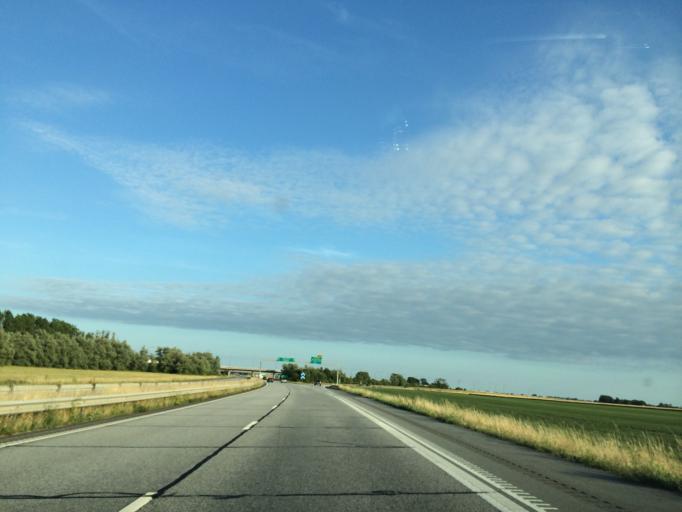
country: SE
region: Skane
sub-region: Vellinge Kommun
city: Vellinge
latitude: 55.4637
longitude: 13.0099
